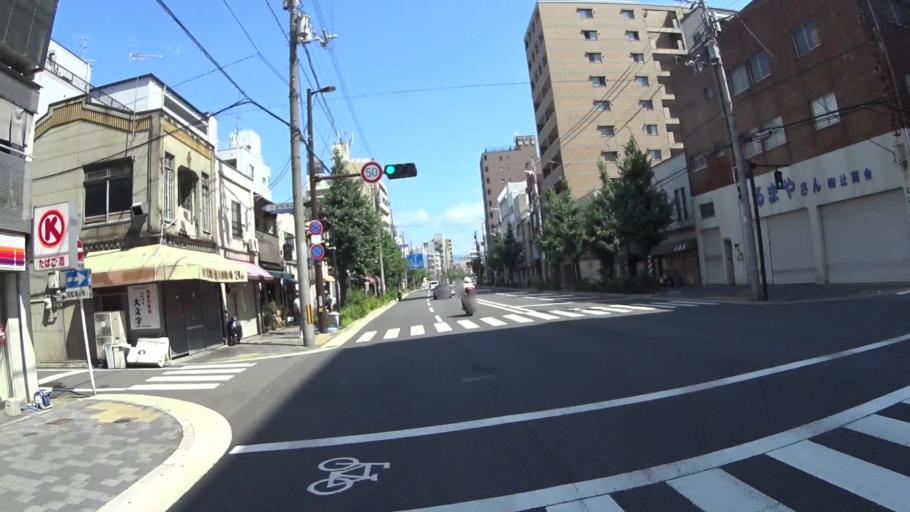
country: JP
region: Kyoto
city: Kyoto
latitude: 35.0152
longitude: 135.7688
